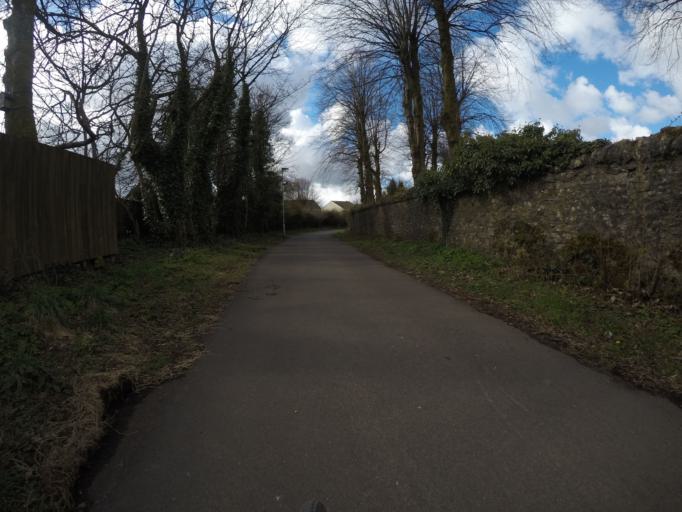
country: GB
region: Scotland
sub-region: North Ayrshire
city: Beith
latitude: 55.7454
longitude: -4.6413
